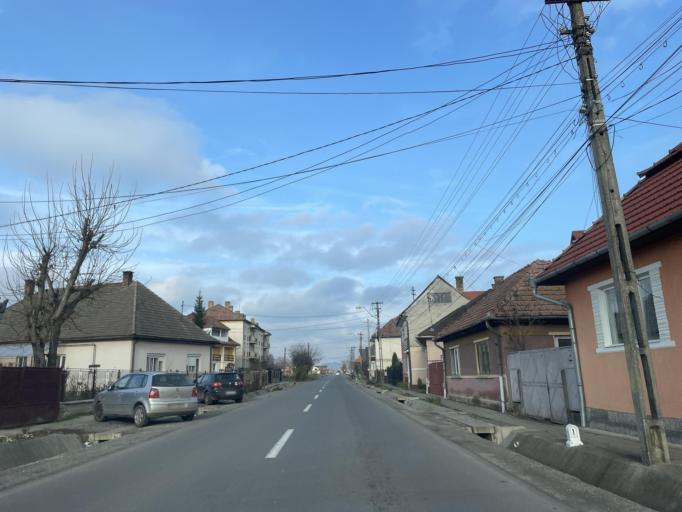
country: RO
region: Mures
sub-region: Municipiul Reghin
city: Reghin
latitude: 46.7881
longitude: 24.7024
